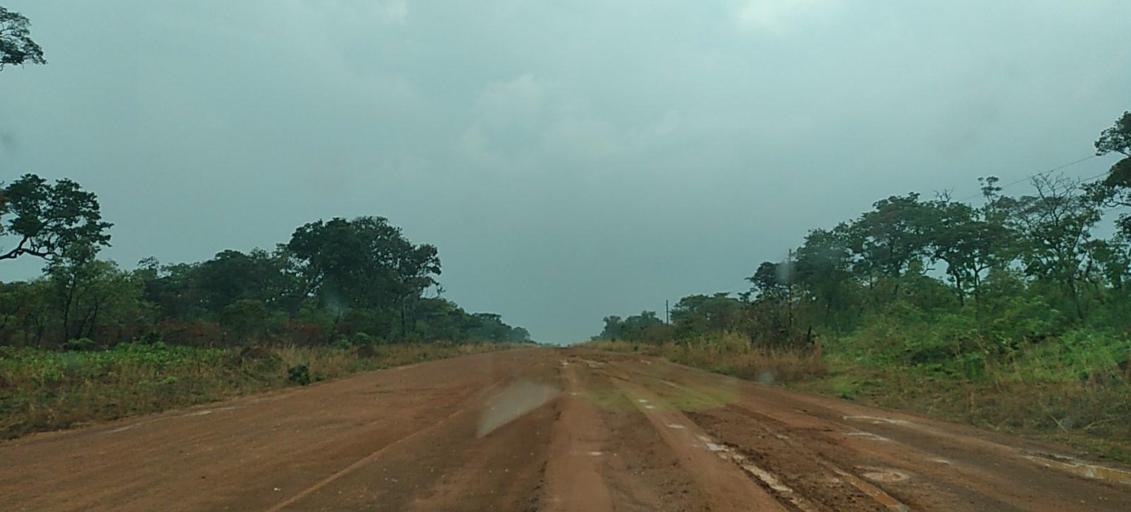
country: ZM
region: North-Western
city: Mwinilunga
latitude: -11.6068
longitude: 24.3961
